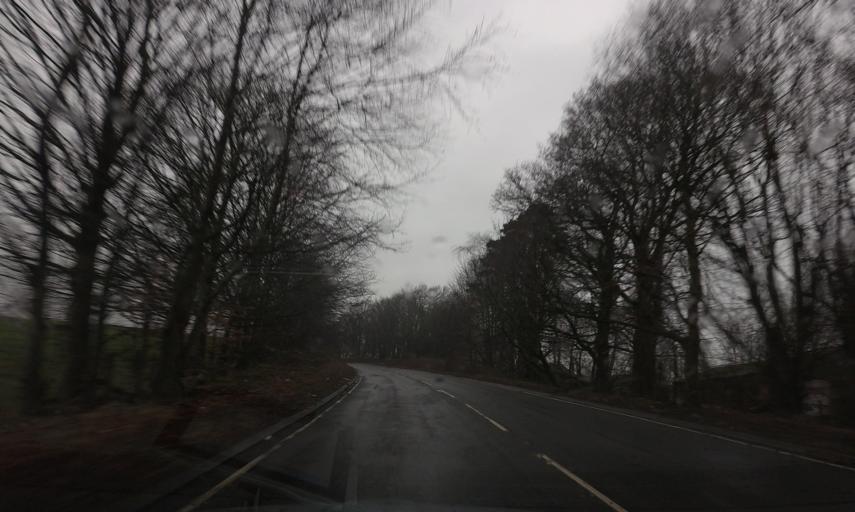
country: GB
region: Scotland
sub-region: East Dunbartonshire
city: Milngavie
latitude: 55.9445
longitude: -4.3493
